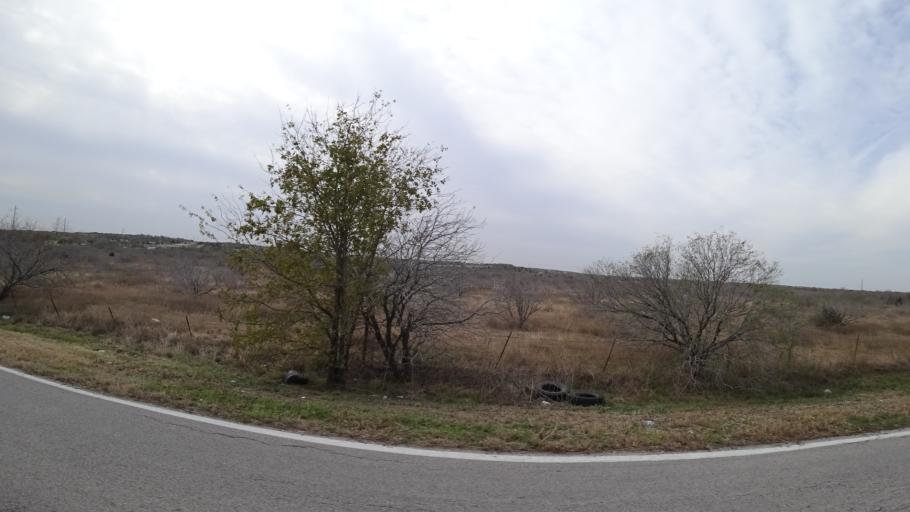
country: US
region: Texas
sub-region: Travis County
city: Onion Creek
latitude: 30.1396
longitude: -97.6816
